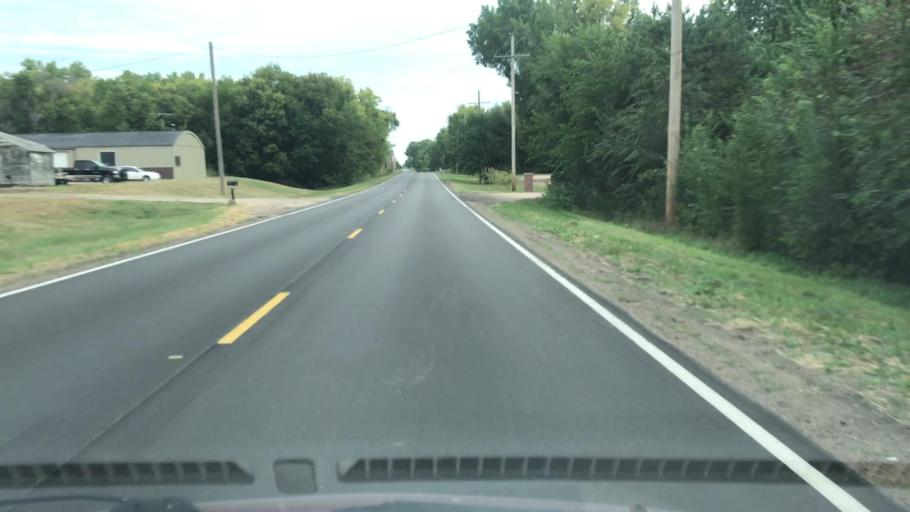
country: US
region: Nebraska
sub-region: Hall County
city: Grand Island
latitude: 40.9213
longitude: -98.3016
